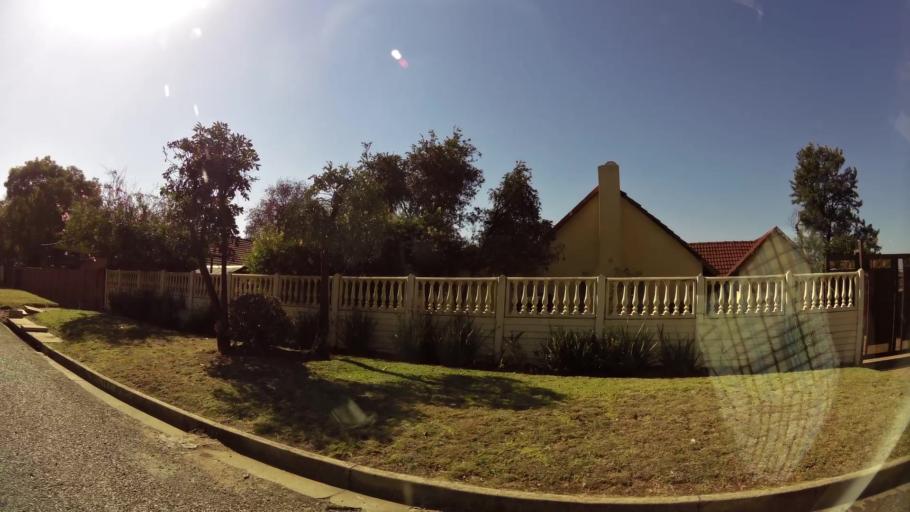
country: ZA
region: Gauteng
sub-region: City of Johannesburg Metropolitan Municipality
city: Modderfontein
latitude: -26.0544
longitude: 28.2073
